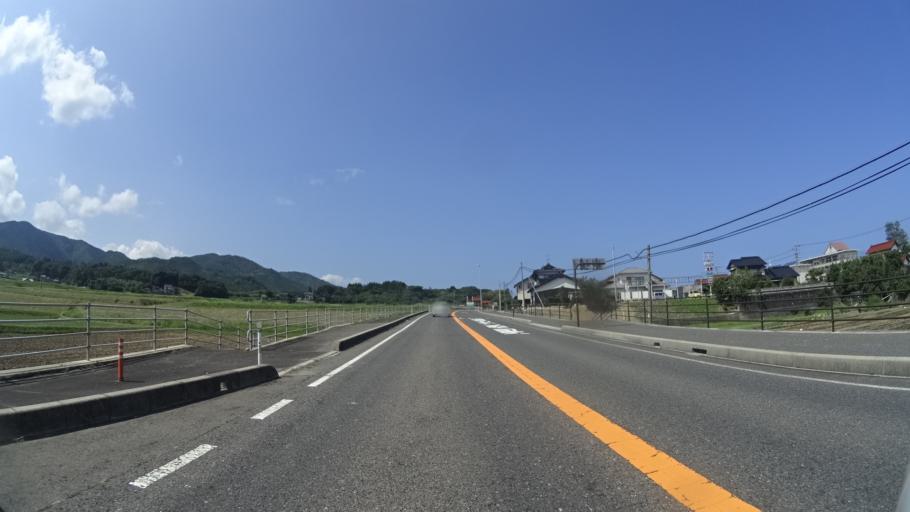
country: JP
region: Shimane
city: Masuda
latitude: 34.6711
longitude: 131.7424
